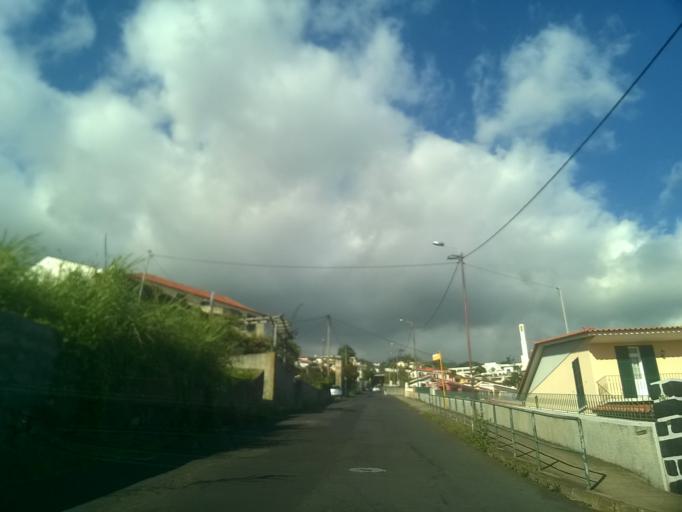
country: PT
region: Madeira
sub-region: Funchal
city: Nossa Senhora do Monte
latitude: 32.6631
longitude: -16.9076
